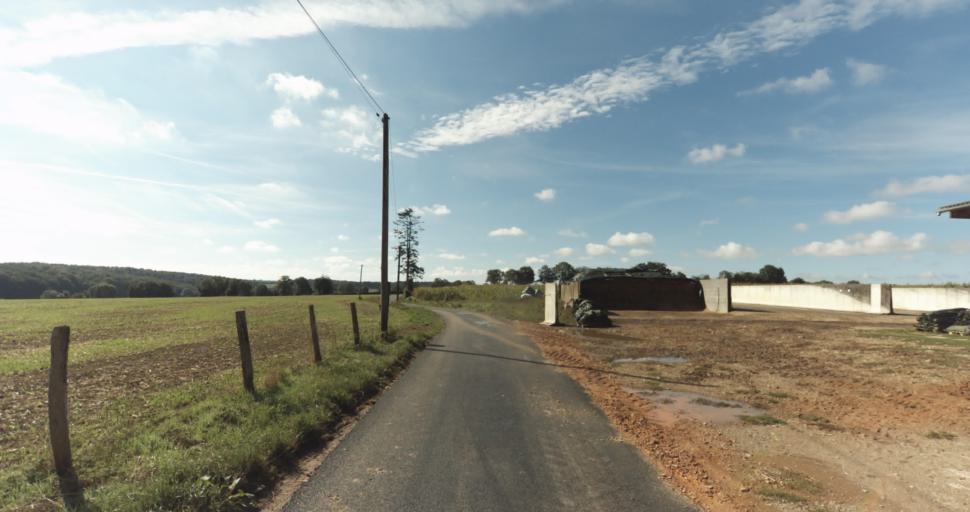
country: FR
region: Lower Normandy
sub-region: Departement du Calvados
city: Orbec
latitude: 48.9428
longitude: 0.3626
